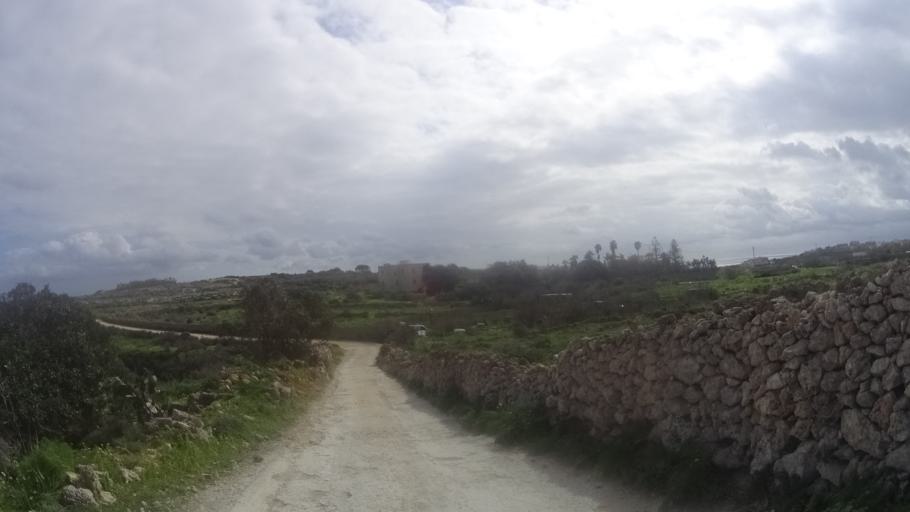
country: MT
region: Il-Qala
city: Qala
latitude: 36.0420
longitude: 14.3179
